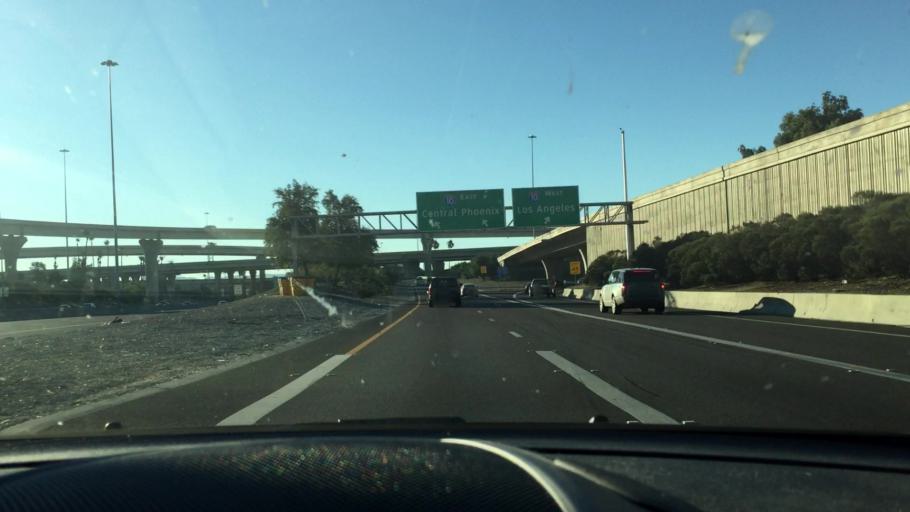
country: US
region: Arizona
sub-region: Maricopa County
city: Phoenix
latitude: 33.4638
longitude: -112.1108
